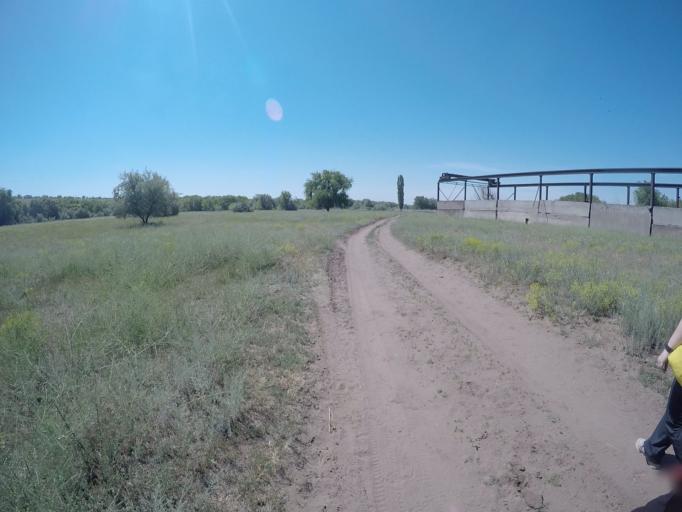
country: RU
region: Saratov
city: Privolzhskiy
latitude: 51.1739
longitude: 45.9214
